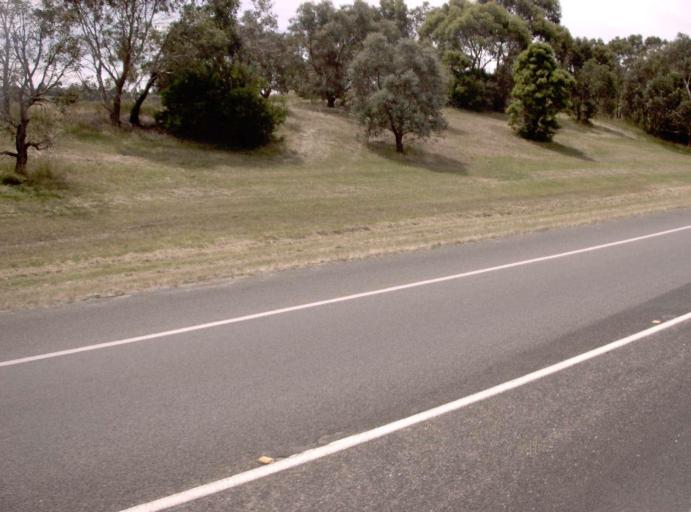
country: AU
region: Victoria
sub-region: Mornington Peninsula
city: Mount Martha
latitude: -38.2985
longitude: 145.0358
